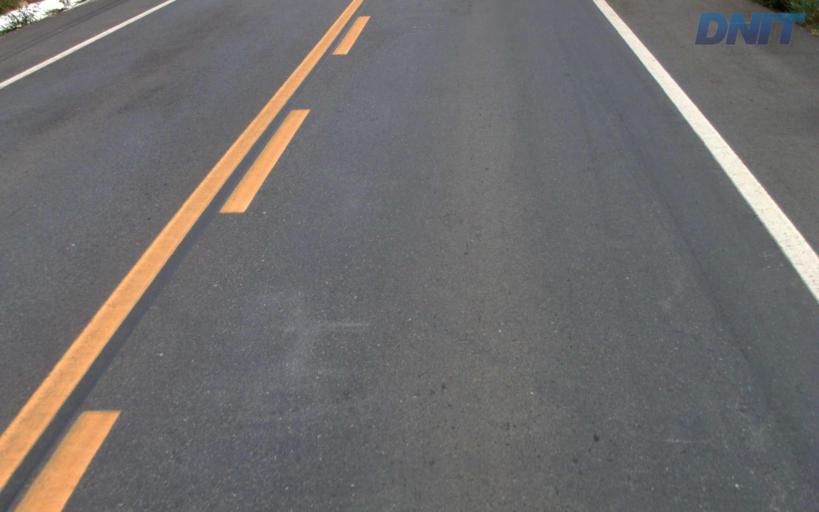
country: BR
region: Minas Gerais
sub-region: Governador Valadares
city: Governador Valadares
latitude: -18.9031
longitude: -42.0034
